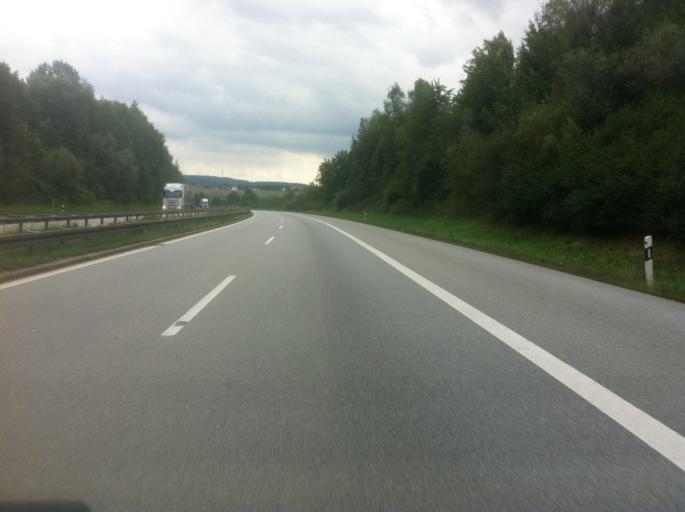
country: DE
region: Bavaria
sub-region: Lower Bavaria
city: Tiefenbach
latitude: 48.5783
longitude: 13.3644
